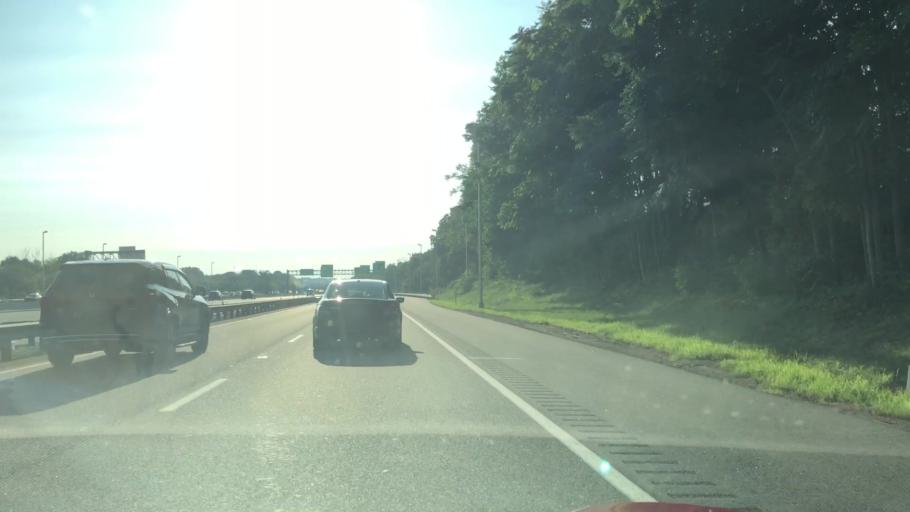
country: US
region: New Jersey
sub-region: Morris County
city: Parsippany
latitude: 40.8628
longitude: -74.4068
